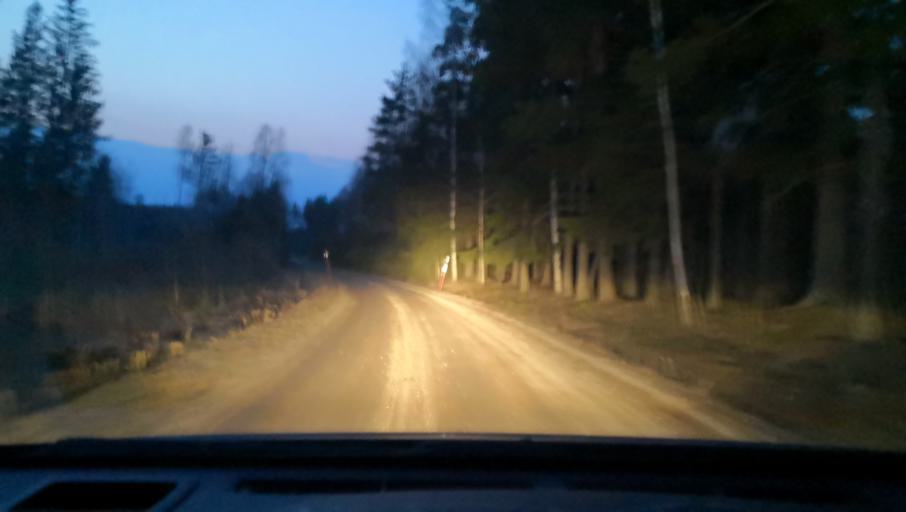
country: SE
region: OErebro
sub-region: Lindesbergs Kommun
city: Frovi
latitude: 59.5950
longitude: 15.4690
